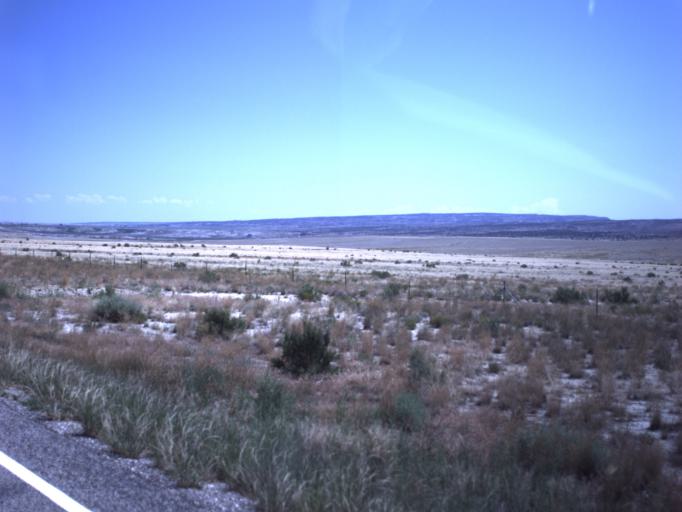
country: US
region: Utah
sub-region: Emery County
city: Ferron
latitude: 38.8347
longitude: -111.3188
